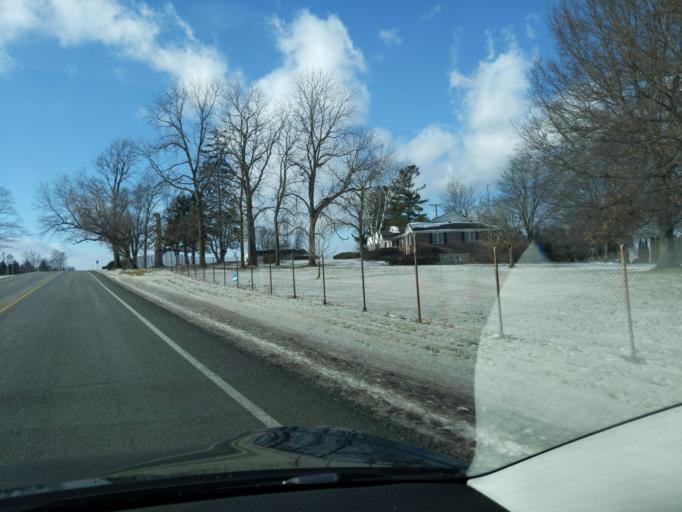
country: US
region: Michigan
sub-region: Ingham County
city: Williamston
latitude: 42.6011
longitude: -84.2804
